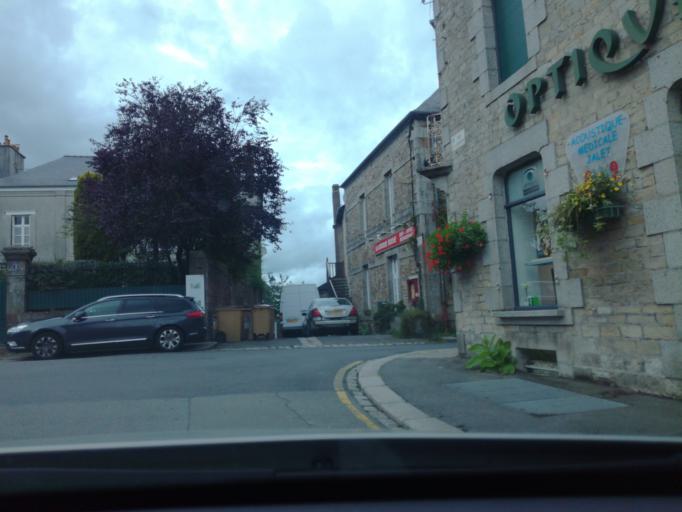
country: FR
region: Brittany
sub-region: Departement d'Ille-et-Vilaine
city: Saint-Aubin-du-Cormier
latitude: 48.2613
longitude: -1.3996
